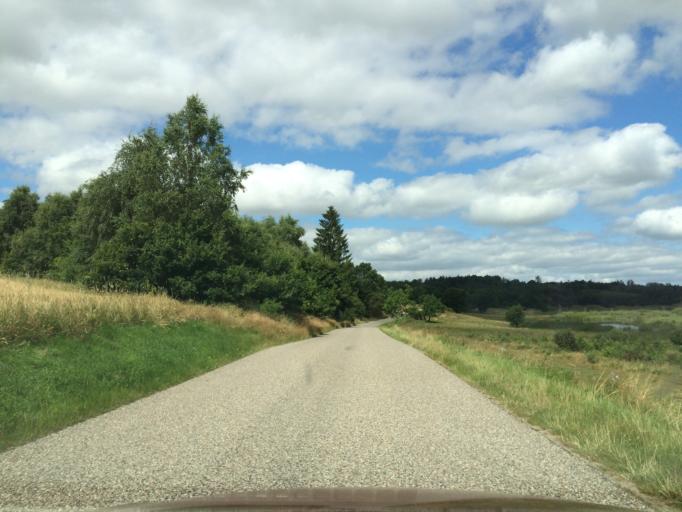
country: DK
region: Central Jutland
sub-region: Silkeborg Kommune
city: Svejbaek
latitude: 56.1966
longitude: 9.6473
